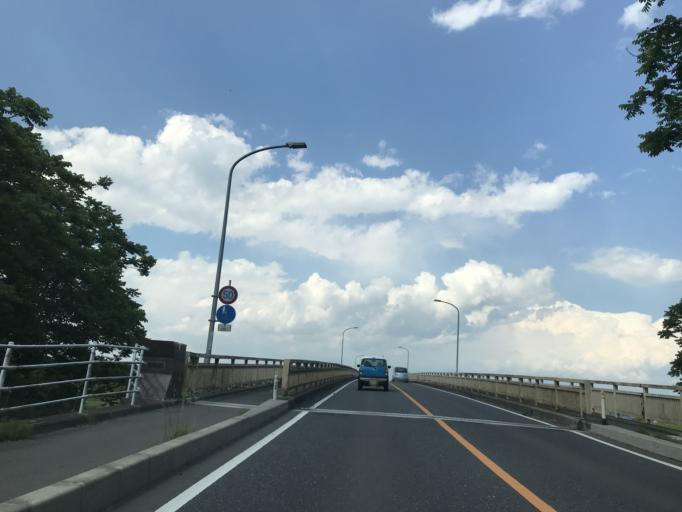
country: JP
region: Miyagi
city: Wakuya
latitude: 38.4965
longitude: 141.1159
